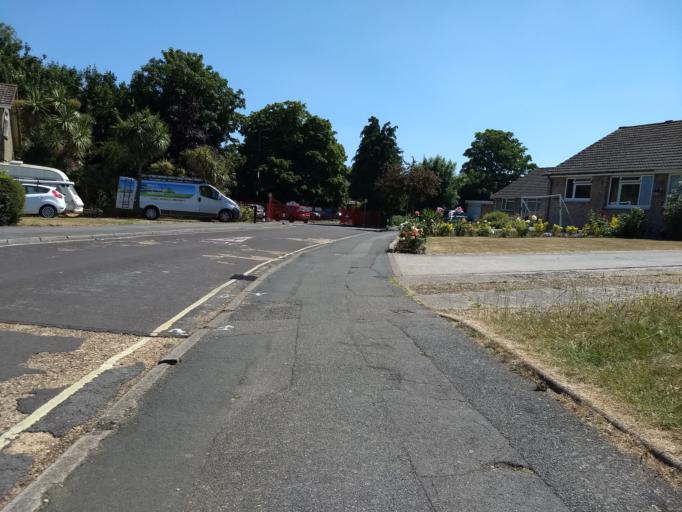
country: GB
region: England
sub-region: Isle of Wight
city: Cowes
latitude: 50.7613
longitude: -1.3058
